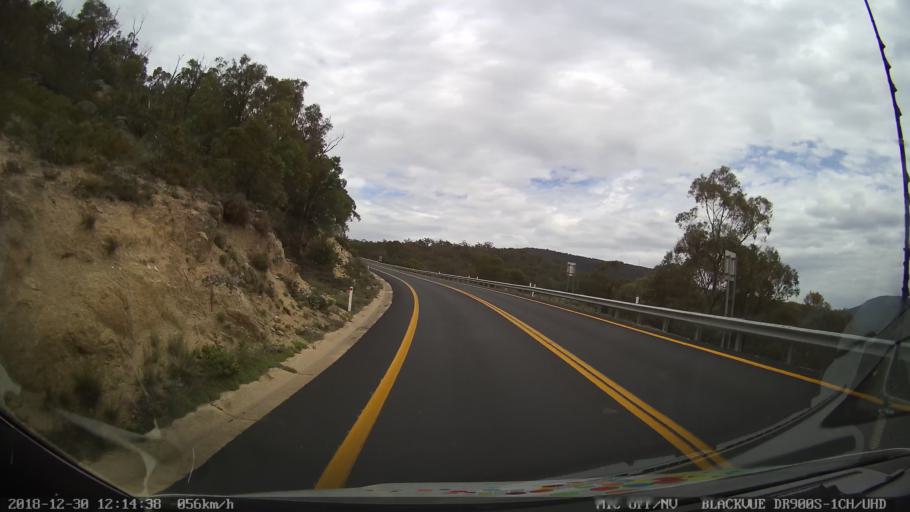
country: AU
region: New South Wales
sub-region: Snowy River
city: Jindabyne
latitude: -36.3420
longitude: 148.5792
